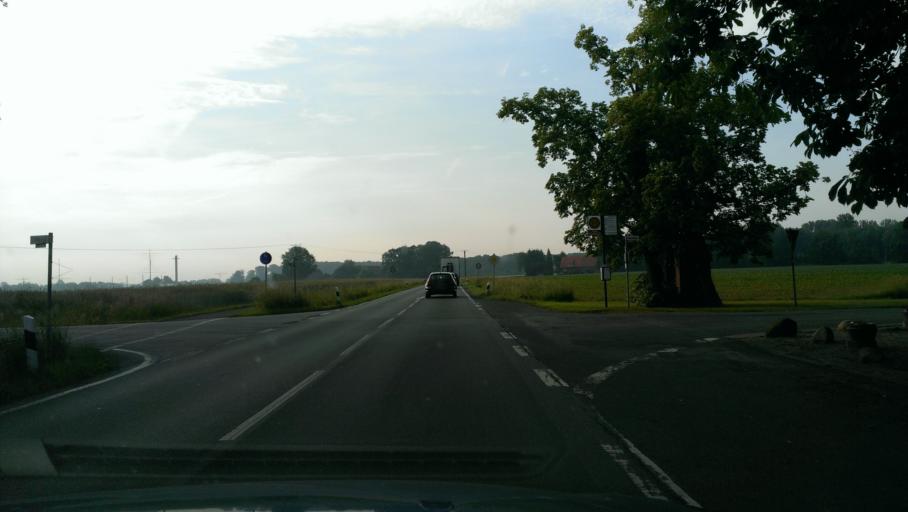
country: DE
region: North Rhine-Westphalia
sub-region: Regierungsbezirk Munster
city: Drensteinfurt
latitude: 51.8896
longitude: 7.7087
